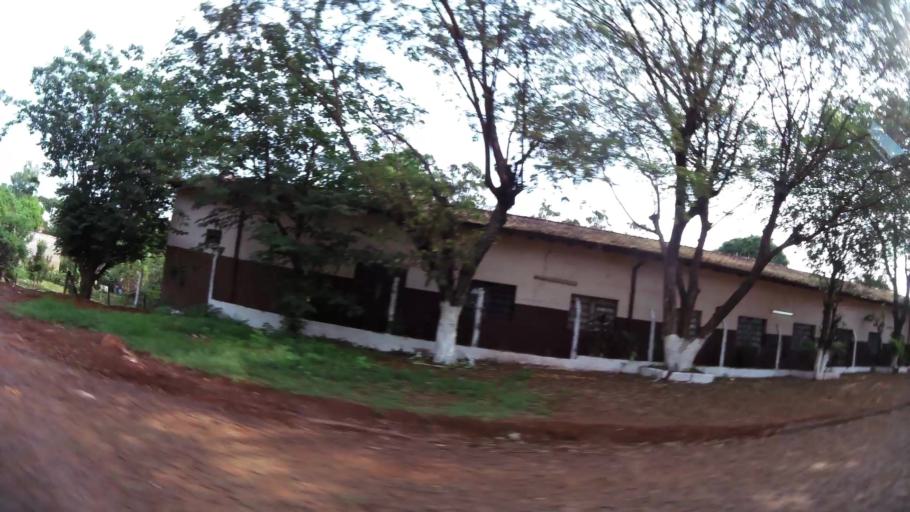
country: PY
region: Alto Parana
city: Ciudad del Este
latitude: -25.4935
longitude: -54.6549
